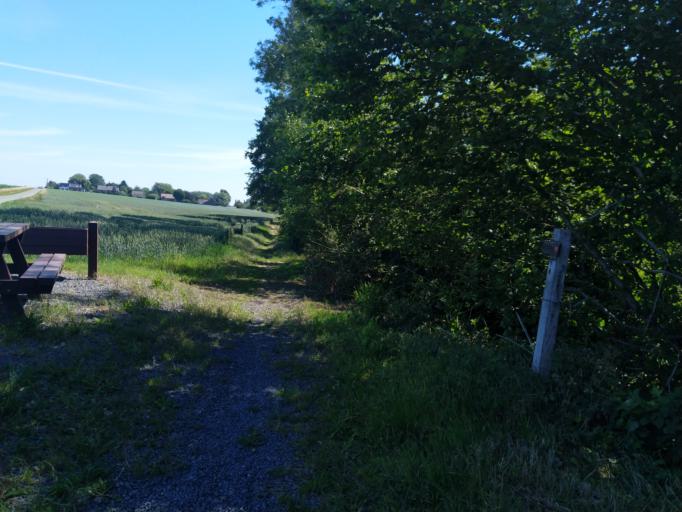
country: BE
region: Wallonia
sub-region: Province du Hainaut
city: Frameries
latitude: 50.3571
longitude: 3.8655
